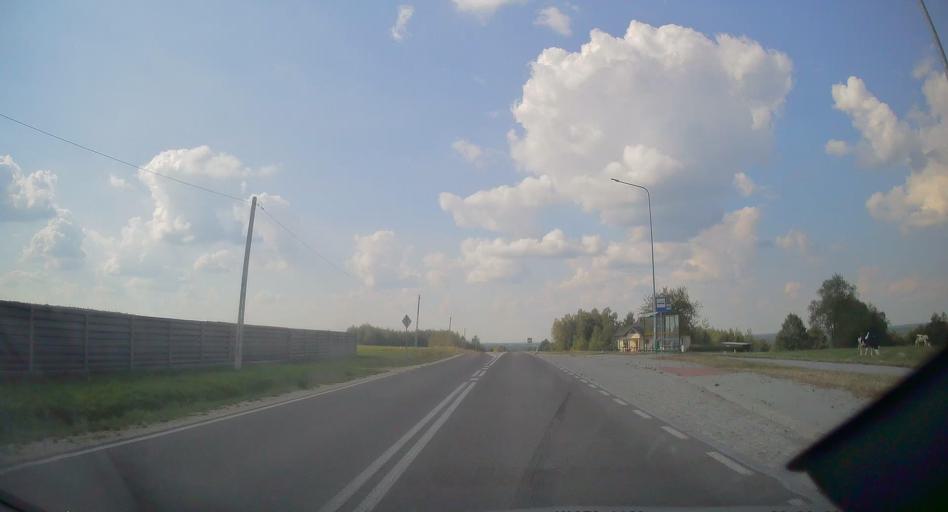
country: PL
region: Swietokrzyskie
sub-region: Powiat konecki
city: Radoszyce
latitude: 51.0347
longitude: 20.2862
